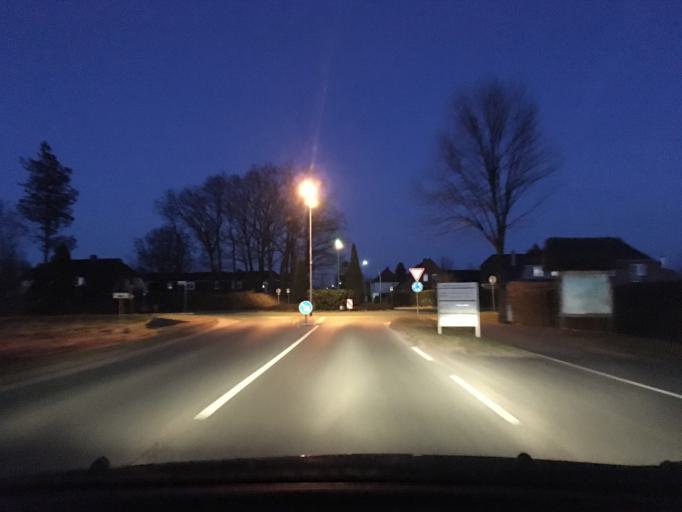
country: DE
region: Lower Saxony
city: Schneverdingen
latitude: 53.1174
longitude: 9.7761
